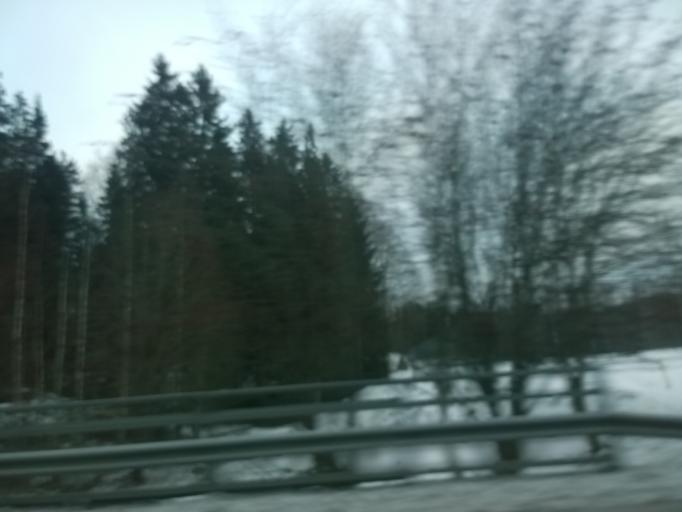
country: FI
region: Pirkanmaa
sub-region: Tampere
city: Tampere
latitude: 61.4418
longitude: 23.8433
